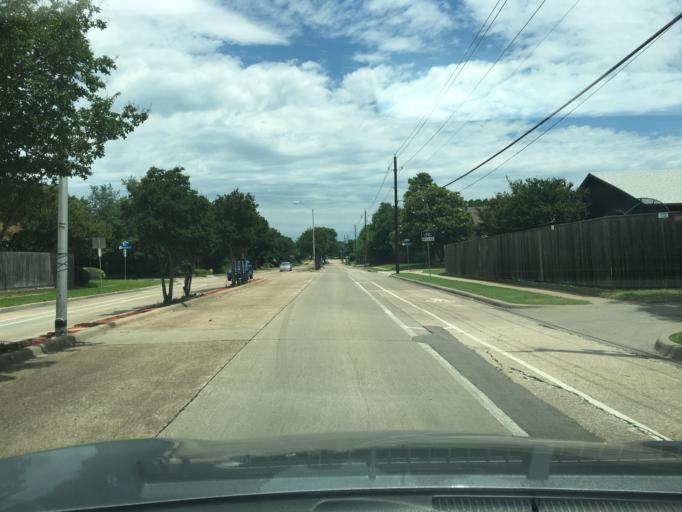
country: US
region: Texas
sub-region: Dallas County
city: Richardson
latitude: 32.9569
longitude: -96.6912
